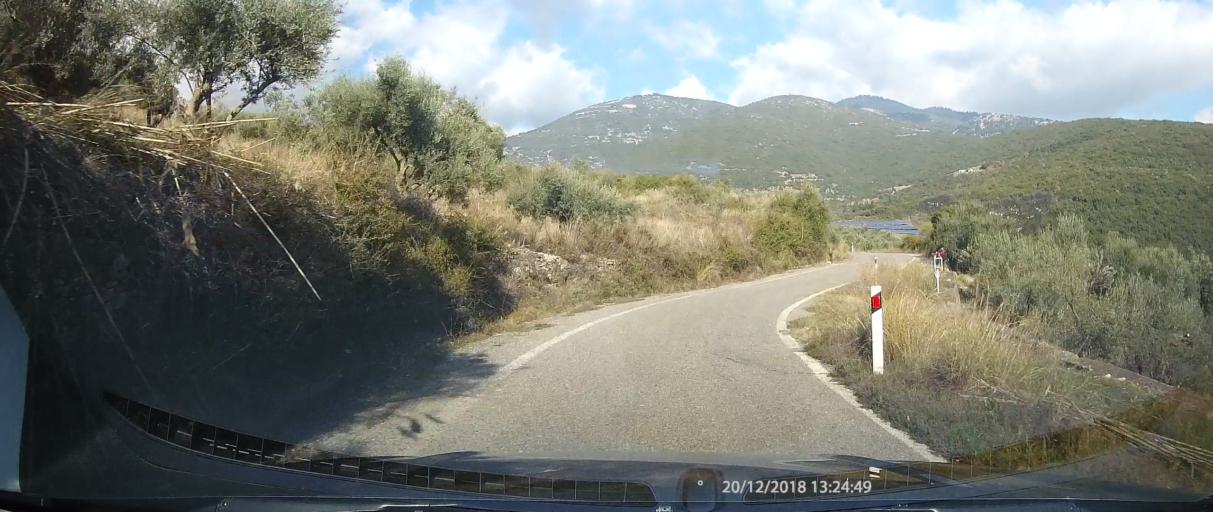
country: GR
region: West Greece
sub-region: Nomos Aitolias kai Akarnanias
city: Paravola
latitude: 38.6211
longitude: 21.5679
